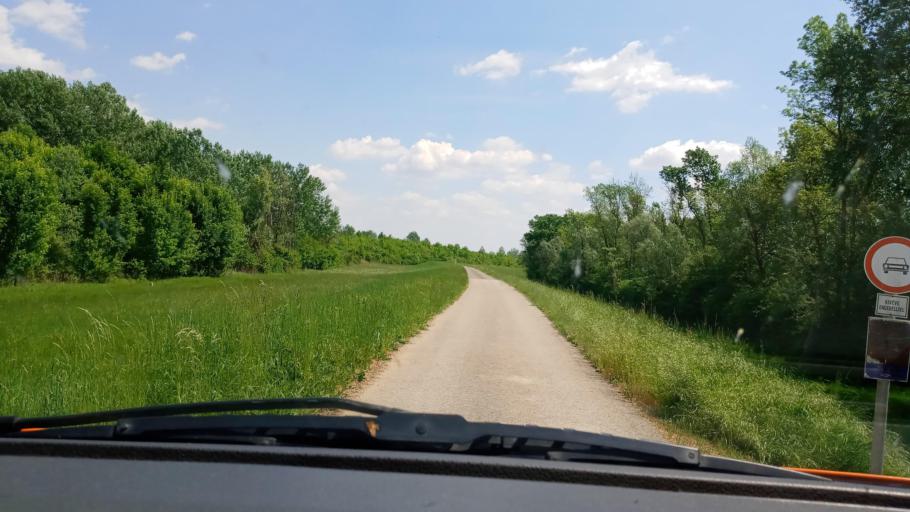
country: HU
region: Baranya
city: Siklos
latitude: 45.7651
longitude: 18.2869
